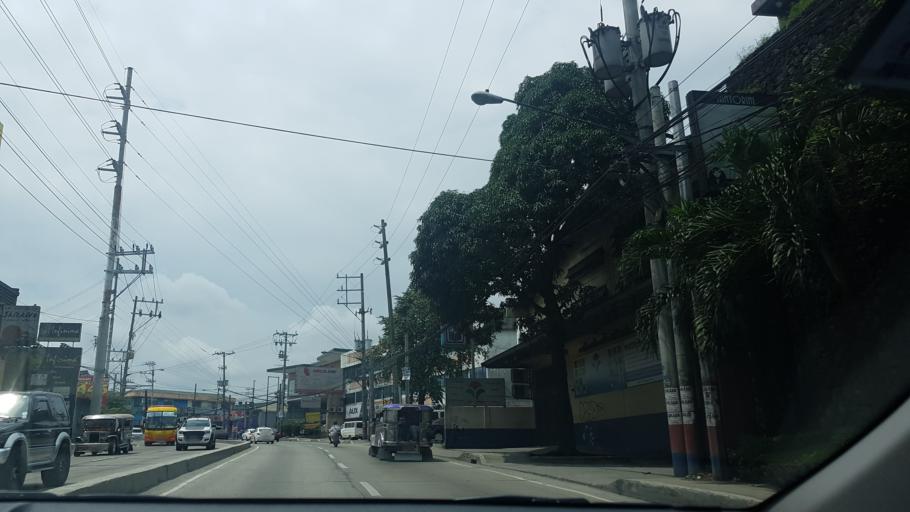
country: PH
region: Metro Manila
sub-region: Caloocan City
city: Niugan
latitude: 14.6691
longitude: 120.9820
